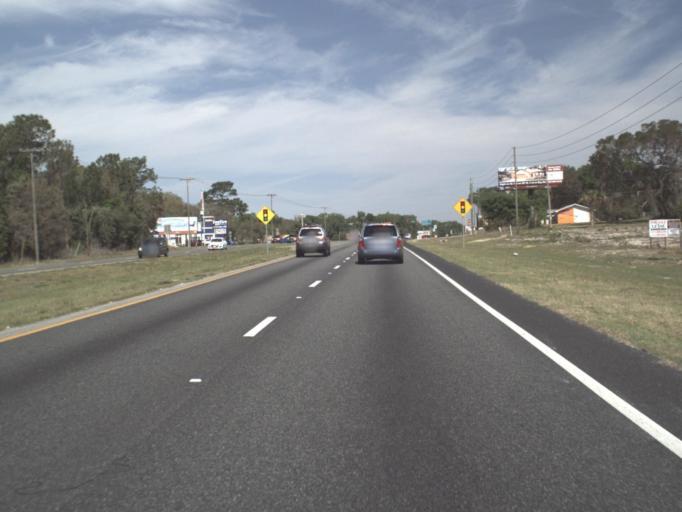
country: US
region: Florida
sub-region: Sumter County
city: The Villages
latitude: 28.9797
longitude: -81.9851
